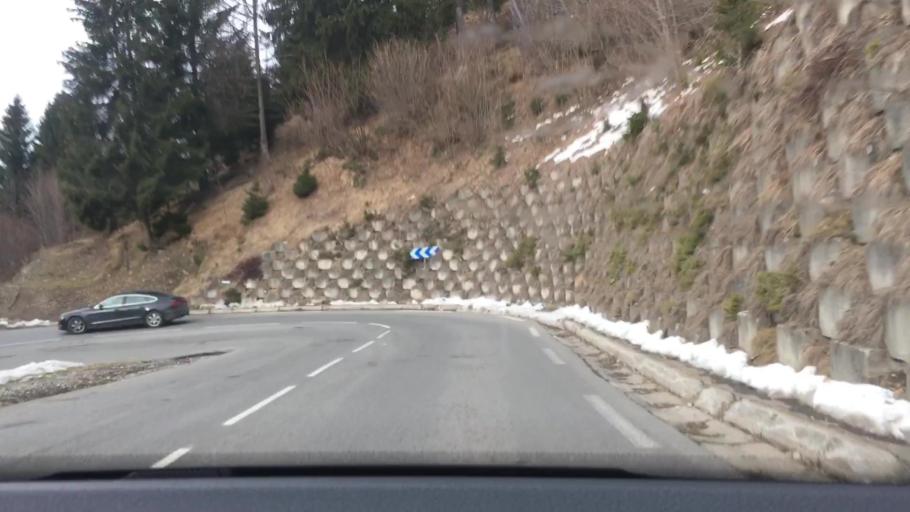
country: FR
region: Rhone-Alpes
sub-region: Departement de la Haute-Savoie
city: Chatel
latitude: 46.2567
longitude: 6.8450
